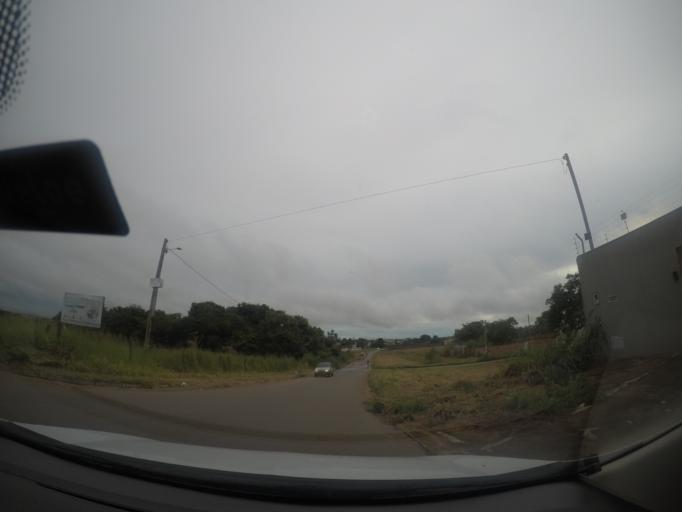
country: BR
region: Goias
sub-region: Aparecida De Goiania
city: Aparecida de Goiania
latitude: -16.7561
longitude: -49.3130
